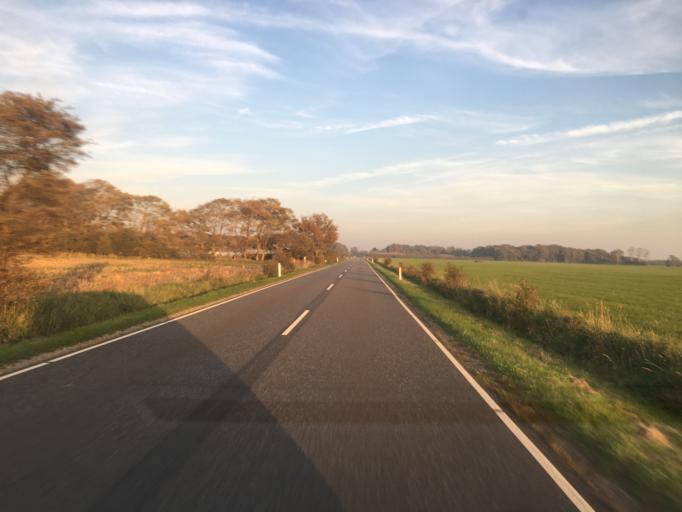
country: DK
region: South Denmark
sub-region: Tonder Kommune
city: Logumkloster
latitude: 55.0478
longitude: 9.0590
